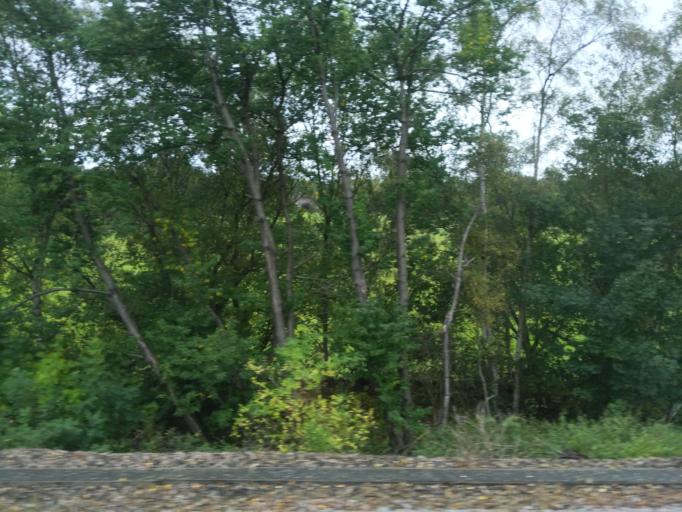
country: GB
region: England
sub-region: Kent
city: Tonbridge
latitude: 51.2076
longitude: 0.2457
